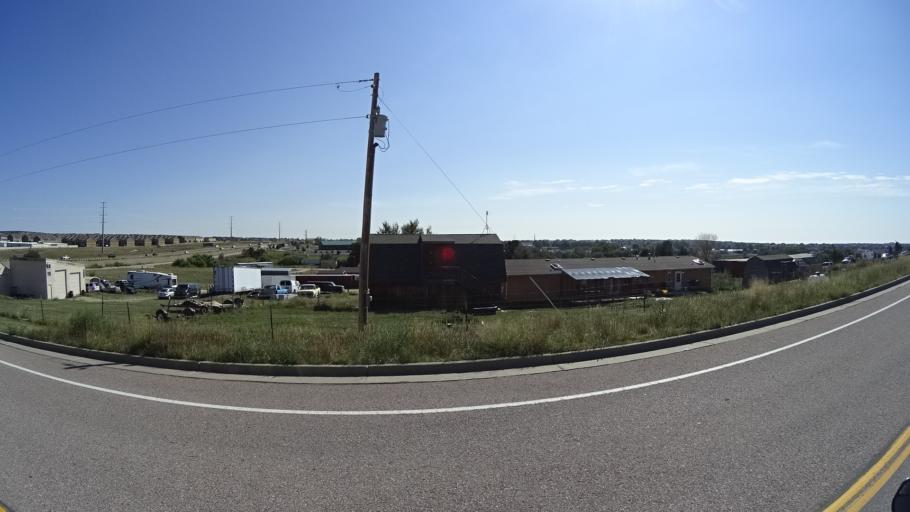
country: US
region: Colorado
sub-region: El Paso County
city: Black Forest
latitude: 38.9396
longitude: -104.6968
